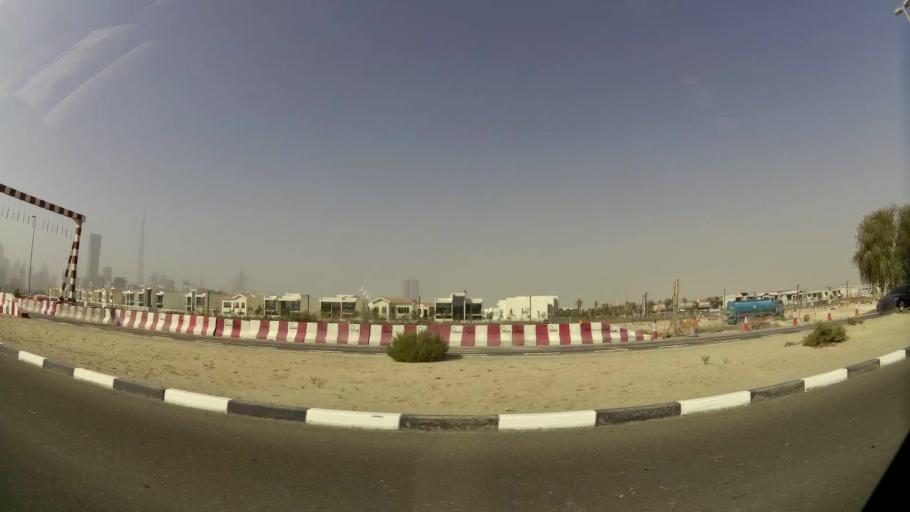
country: AE
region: Dubai
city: Dubai
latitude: 25.1632
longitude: 55.2723
